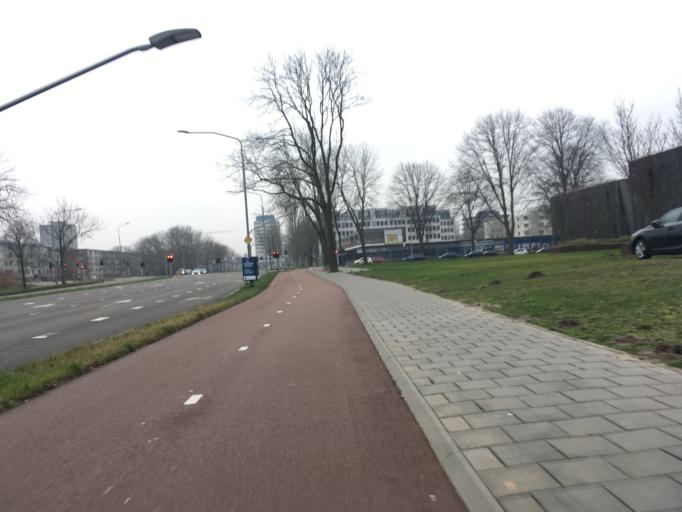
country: NL
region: North Holland
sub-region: Gemeente Haarlem
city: Haarlem
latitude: 52.3654
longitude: 4.6541
